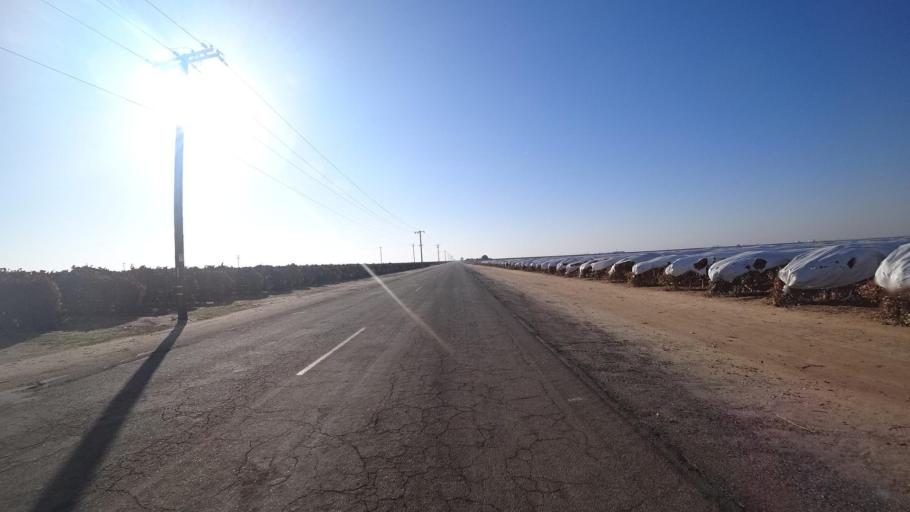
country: US
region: California
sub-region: Kern County
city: McFarland
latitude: 35.7343
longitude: -119.1695
